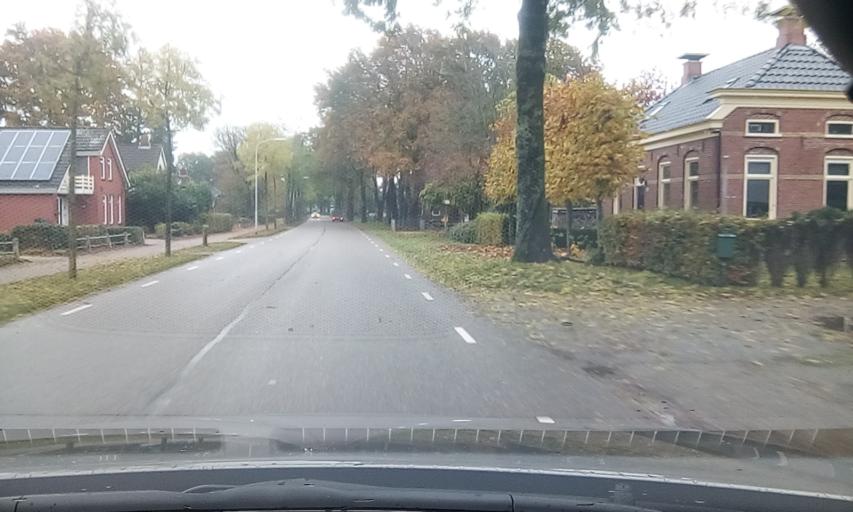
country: NL
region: Groningen
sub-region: Gemeente Haren
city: Haren
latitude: 53.2092
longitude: 6.6749
